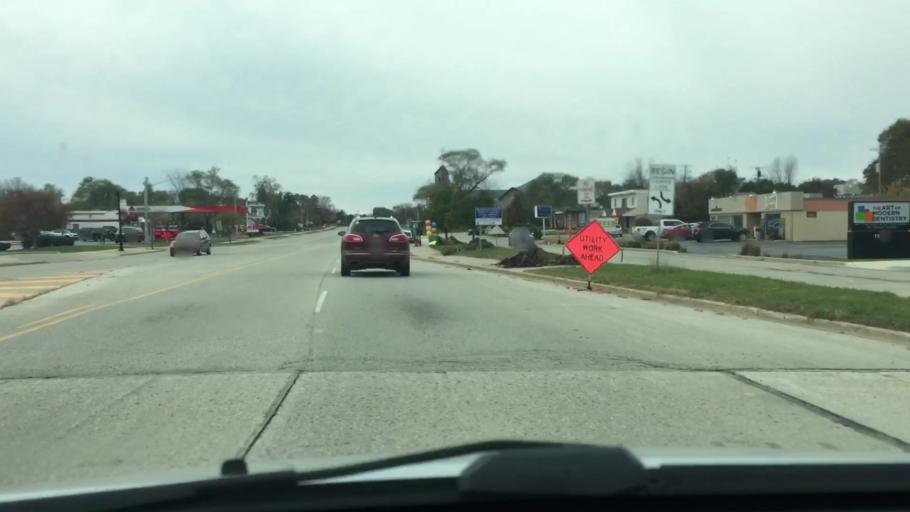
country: US
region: Wisconsin
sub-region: Waukesha County
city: New Berlin
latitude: 42.9753
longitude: -88.1100
